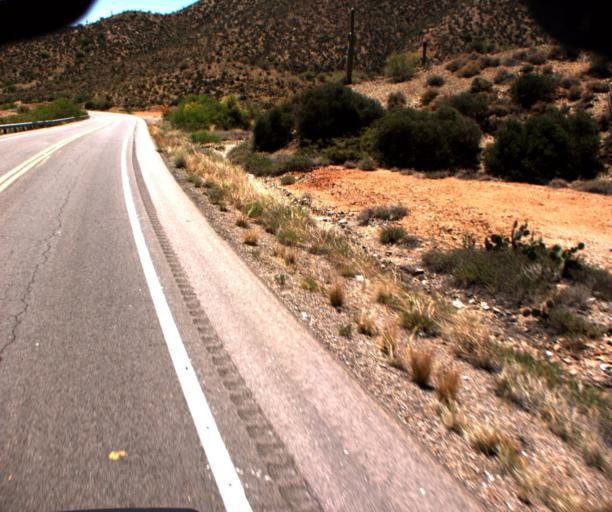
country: US
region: Arizona
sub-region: Pinal County
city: Superior
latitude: 33.1739
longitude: -111.0173
